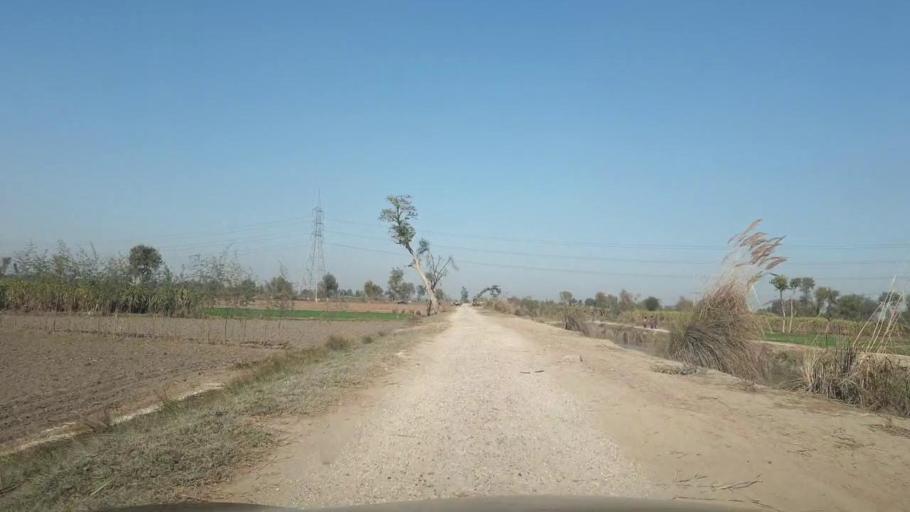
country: PK
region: Sindh
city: Ghotki
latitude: 27.9897
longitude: 69.4279
